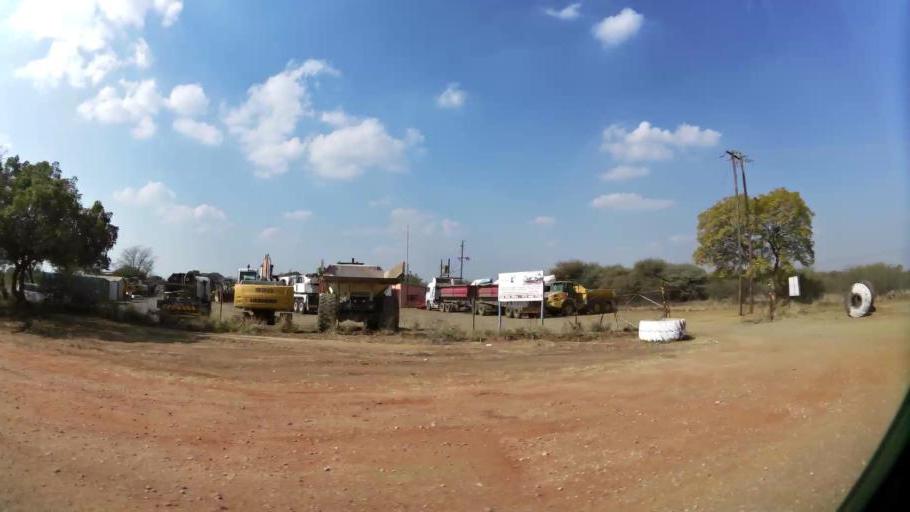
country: ZA
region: North-West
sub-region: Bojanala Platinum District Municipality
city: Mogwase
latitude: -25.4813
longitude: 27.0864
